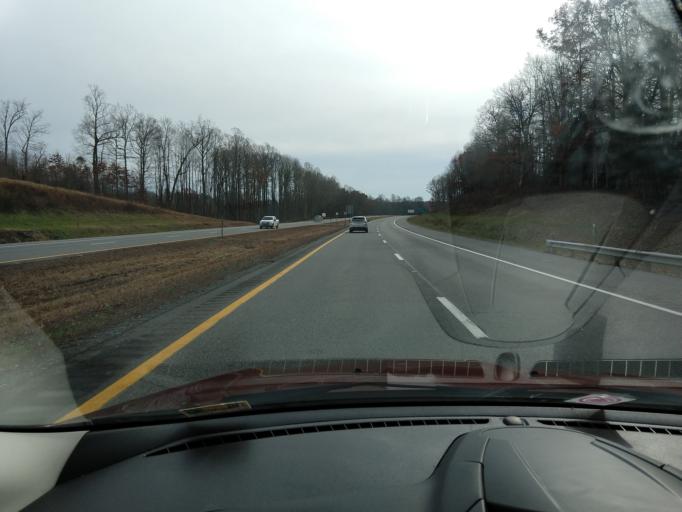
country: US
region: West Virginia
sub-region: Nicholas County
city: Summersville
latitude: 38.2891
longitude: -80.8324
